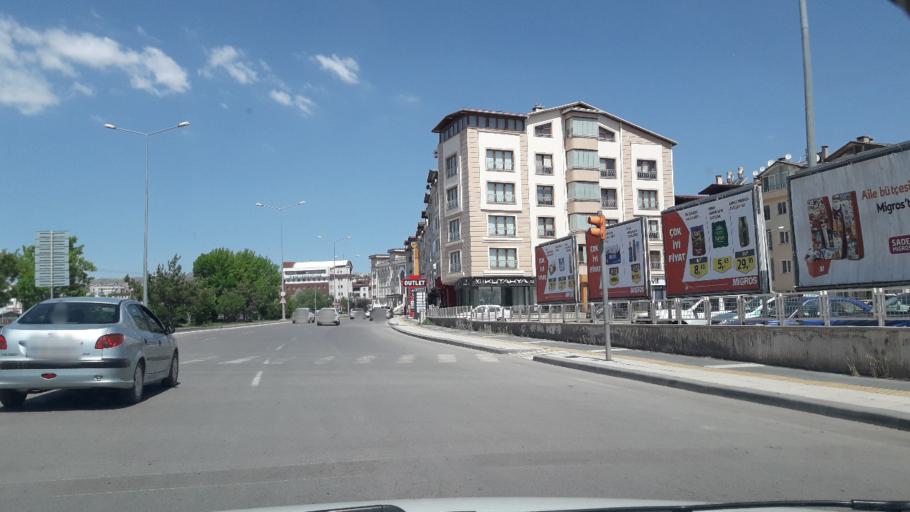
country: TR
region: Sivas
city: Sivas
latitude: 39.7397
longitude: 37.0162
